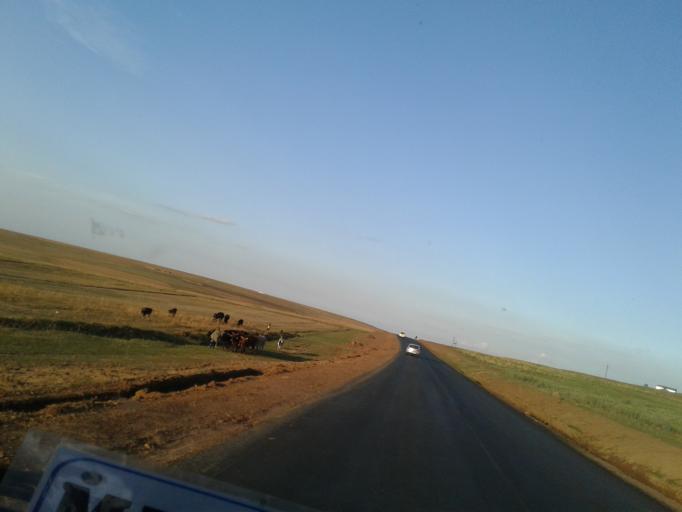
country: LS
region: Maseru
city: Maseru
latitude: -29.3102
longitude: 27.5998
